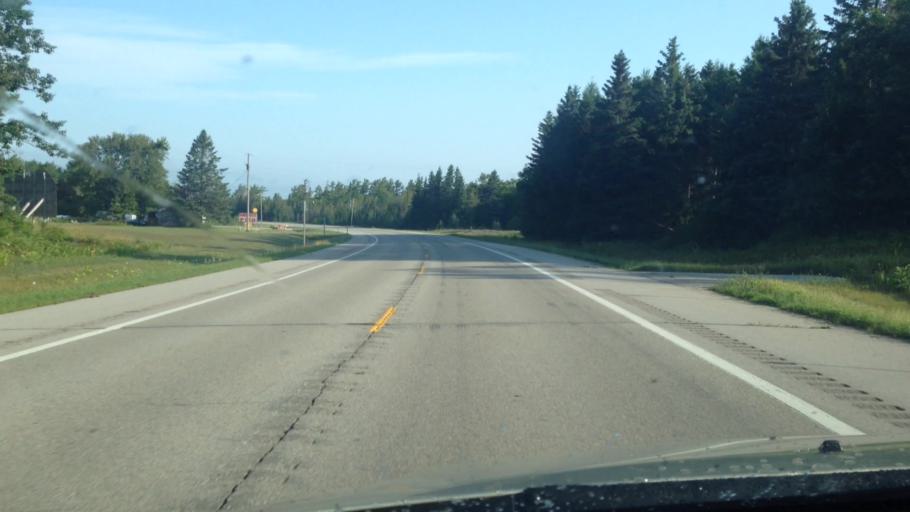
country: US
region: Michigan
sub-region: Mackinac County
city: Saint Ignace
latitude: 45.8951
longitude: -84.8331
